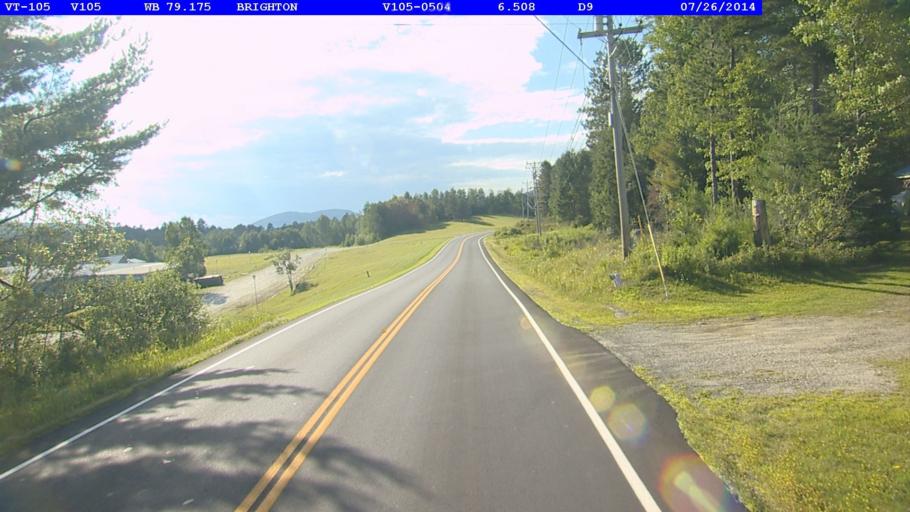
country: US
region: Vermont
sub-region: Caledonia County
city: Lyndonville
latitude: 44.8040
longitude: -71.8472
